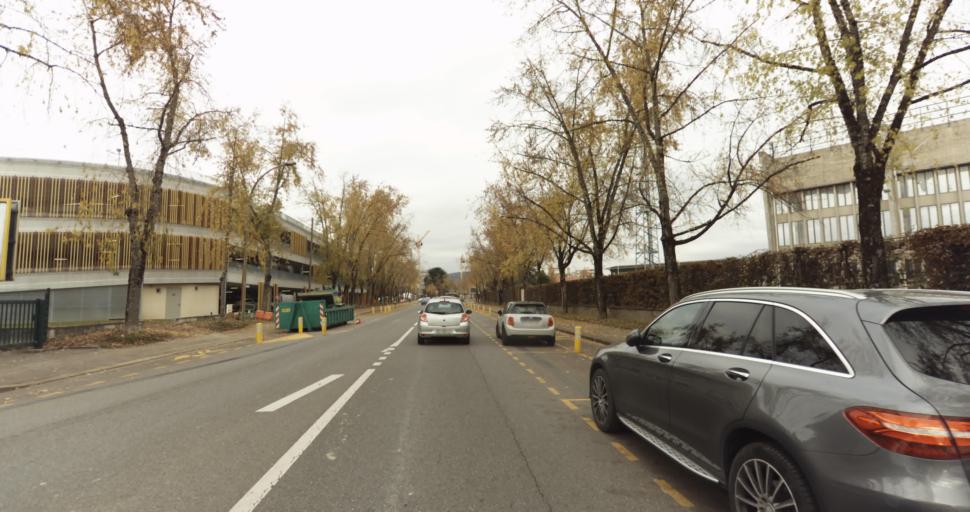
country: FR
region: Rhone-Alpes
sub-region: Departement de la Haute-Savoie
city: Annecy
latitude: 45.9166
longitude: 6.1163
